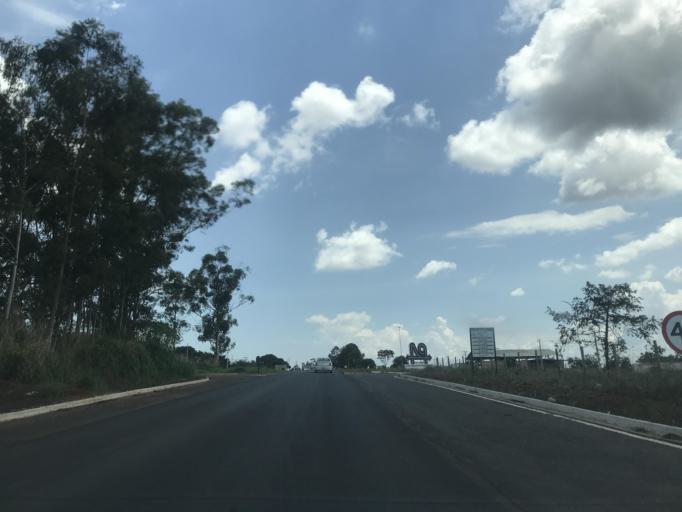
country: BR
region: Goias
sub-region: Bela Vista De Goias
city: Bela Vista de Goias
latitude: -17.0675
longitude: -48.6579
